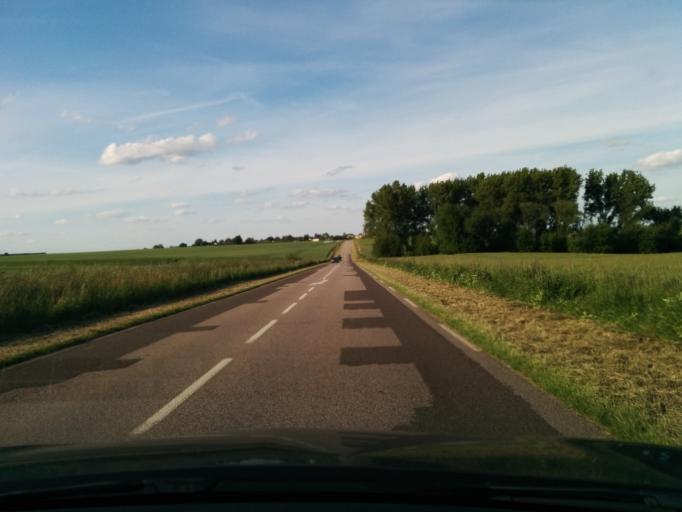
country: FR
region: Haute-Normandie
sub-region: Departement de l'Eure
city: Les Andelys
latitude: 49.2986
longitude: 1.4235
